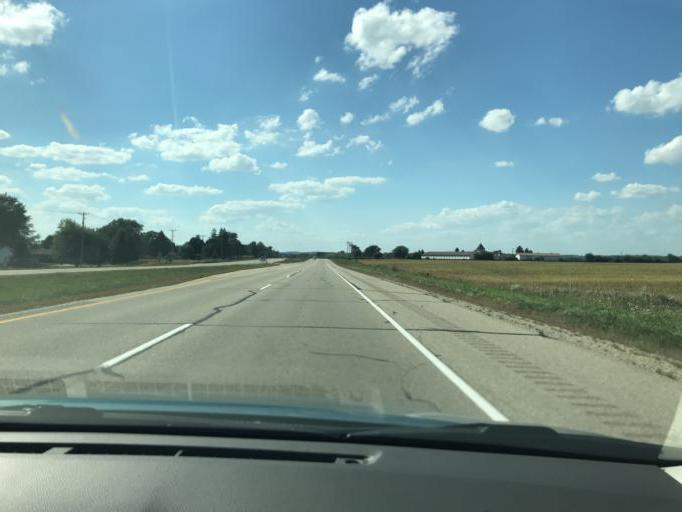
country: US
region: Wisconsin
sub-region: Walworth County
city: Pell Lake
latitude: 42.5968
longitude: -88.3698
